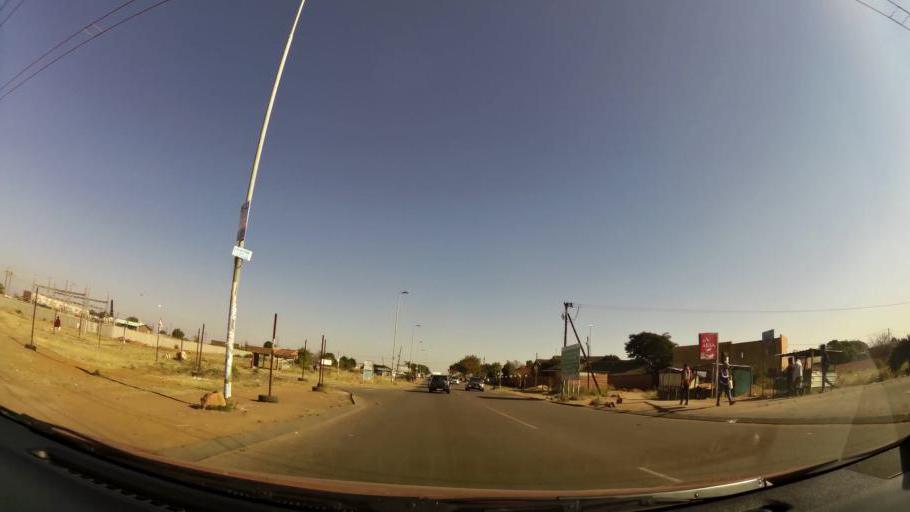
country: ZA
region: Gauteng
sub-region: City of Tshwane Metropolitan Municipality
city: Mabopane
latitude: -25.5474
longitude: 28.0950
